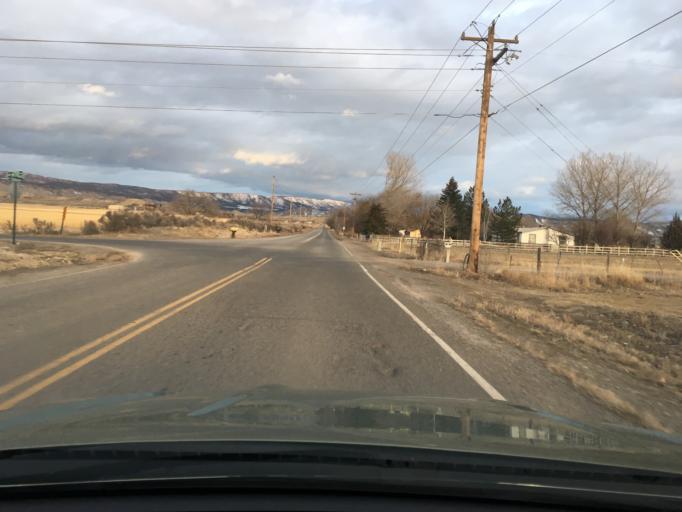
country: US
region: Colorado
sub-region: Montrose County
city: Montrose
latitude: 38.4744
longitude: -107.8345
